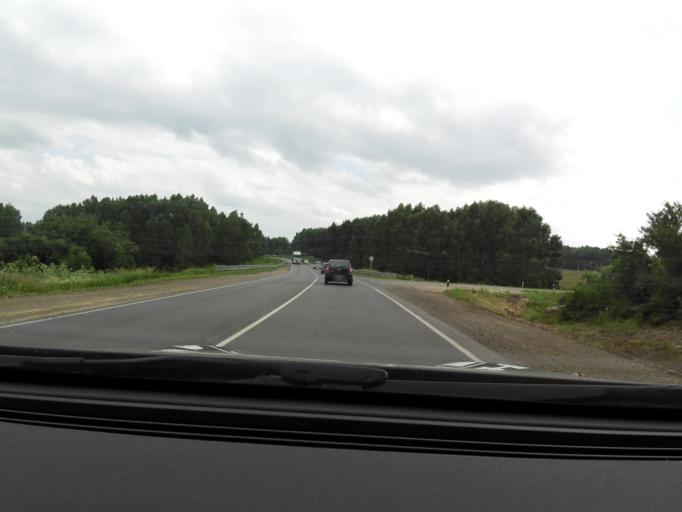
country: RU
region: Perm
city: Kungur
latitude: 57.4525
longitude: 56.7748
